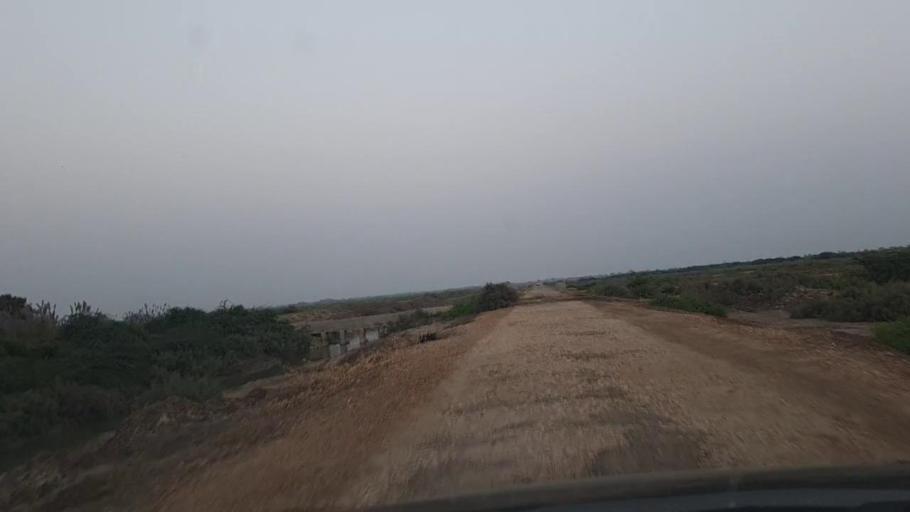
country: PK
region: Sindh
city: Mirpur Sakro
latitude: 24.6349
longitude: 67.7062
